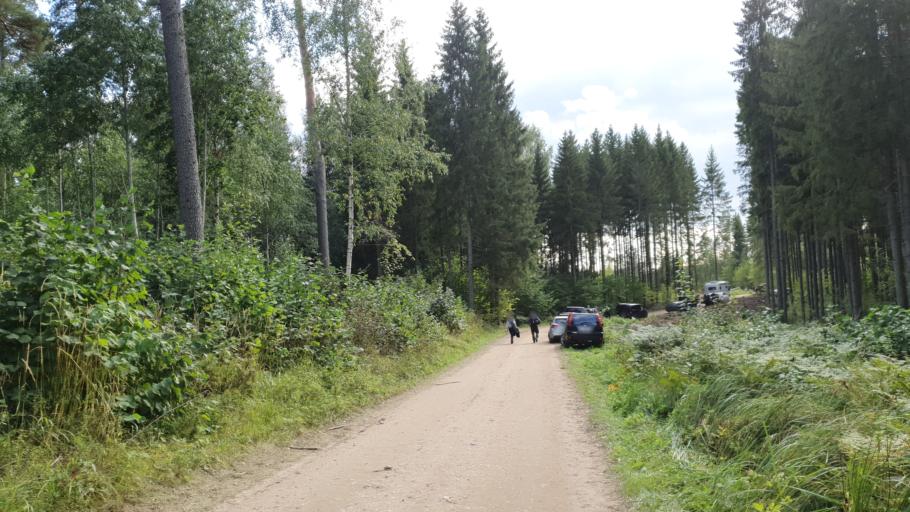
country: EE
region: Tartu
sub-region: UElenurme vald
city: Ulenurme
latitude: 58.1274
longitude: 26.7433
